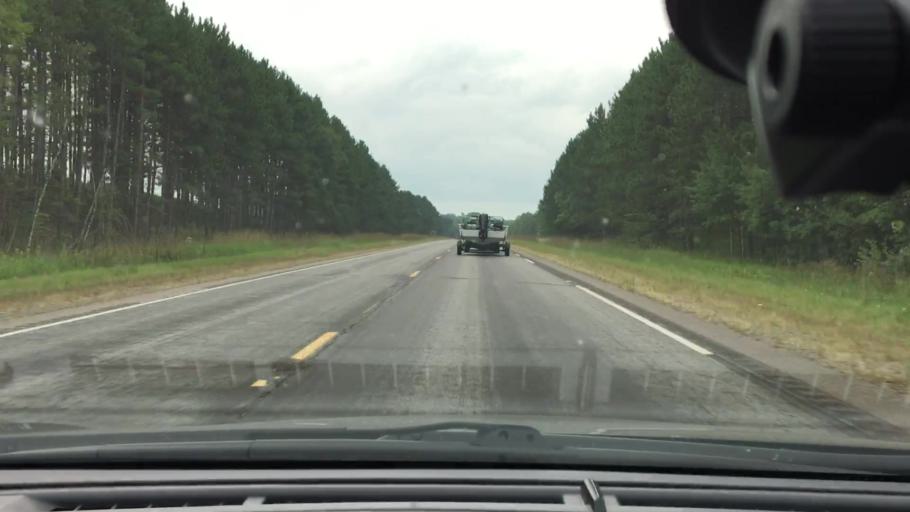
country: US
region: Minnesota
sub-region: Crow Wing County
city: Crosby
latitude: 46.6357
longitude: -93.9488
